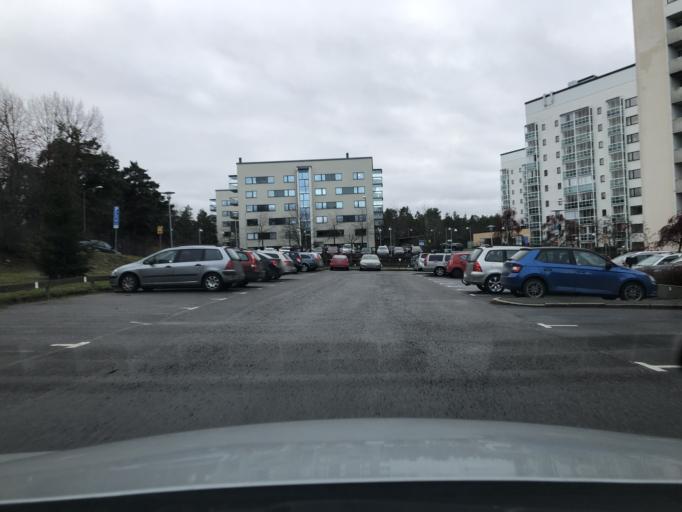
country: SE
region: Stockholm
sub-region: Stockholms Kommun
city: Arsta
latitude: 59.3015
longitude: 18.0531
